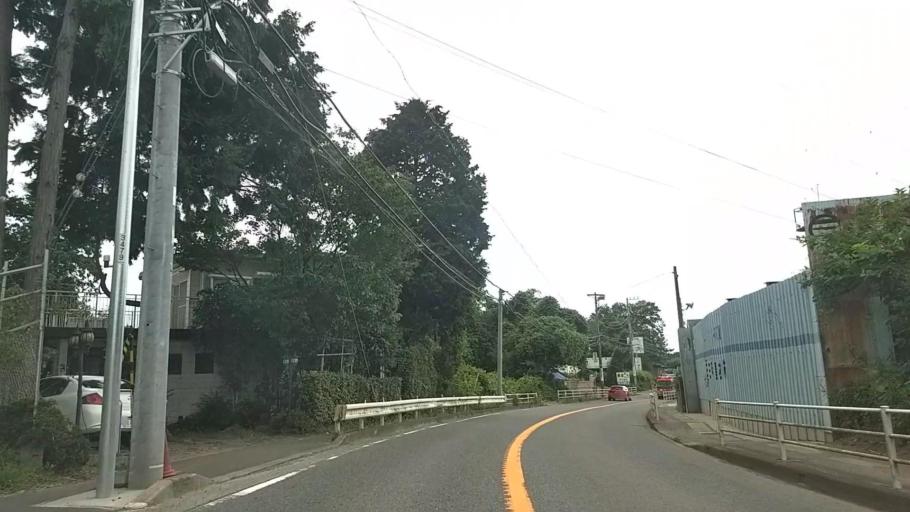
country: JP
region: Kanagawa
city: Chigasaki
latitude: 35.3698
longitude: 139.4197
